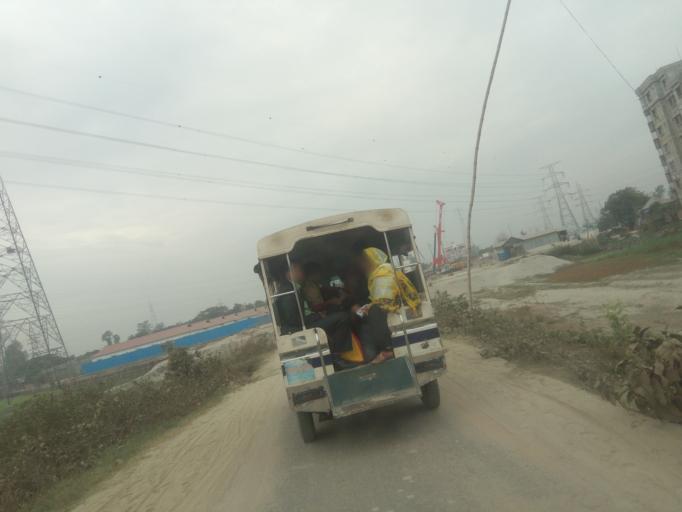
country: BD
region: Dhaka
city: Narayanganj
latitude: 23.5874
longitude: 90.5050
